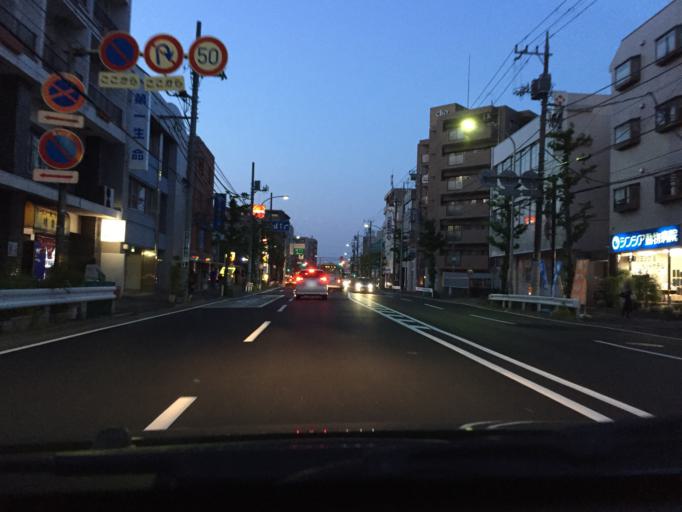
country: JP
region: Kanagawa
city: Yokohama
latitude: 35.4158
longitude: 139.5981
